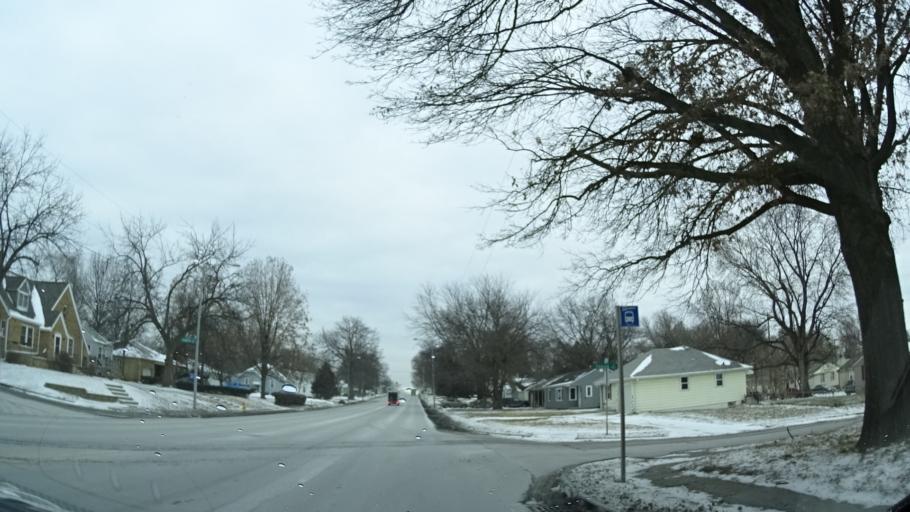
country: US
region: Nebraska
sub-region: Douglas County
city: Omaha
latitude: 41.2316
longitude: -95.9758
